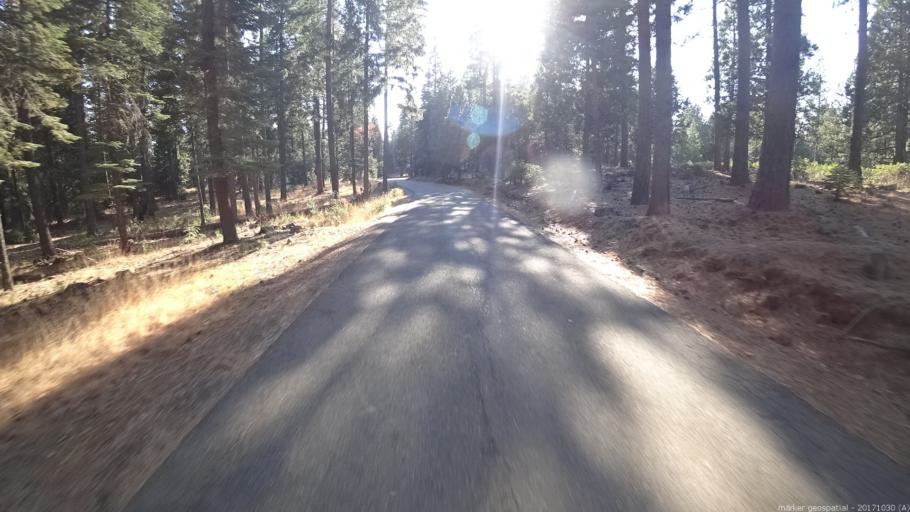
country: US
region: California
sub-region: Shasta County
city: Shingletown
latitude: 40.5409
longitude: -121.7365
